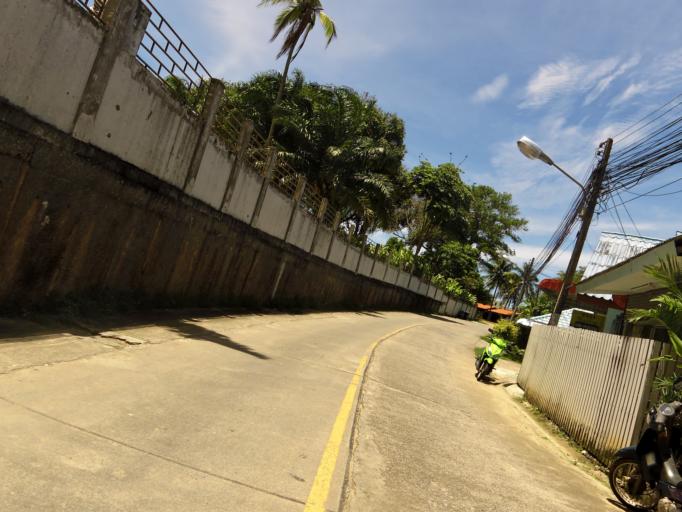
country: TH
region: Phuket
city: Ban Karon
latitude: 7.8484
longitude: 98.3000
